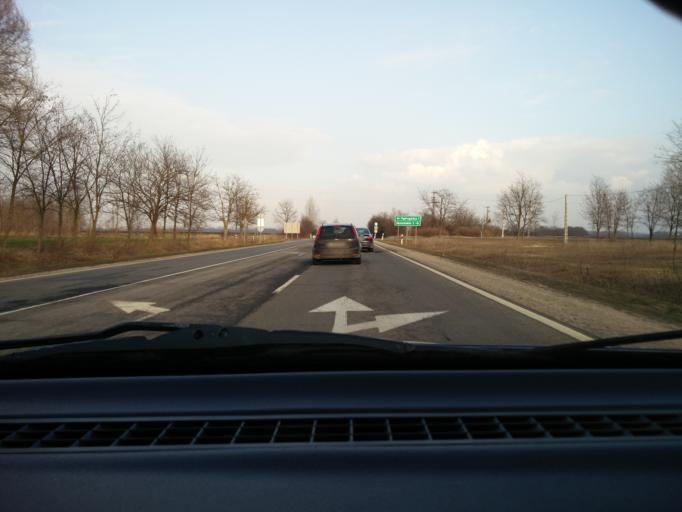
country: HU
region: Pest
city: Nyaregyhaza
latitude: 47.2551
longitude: 19.5205
